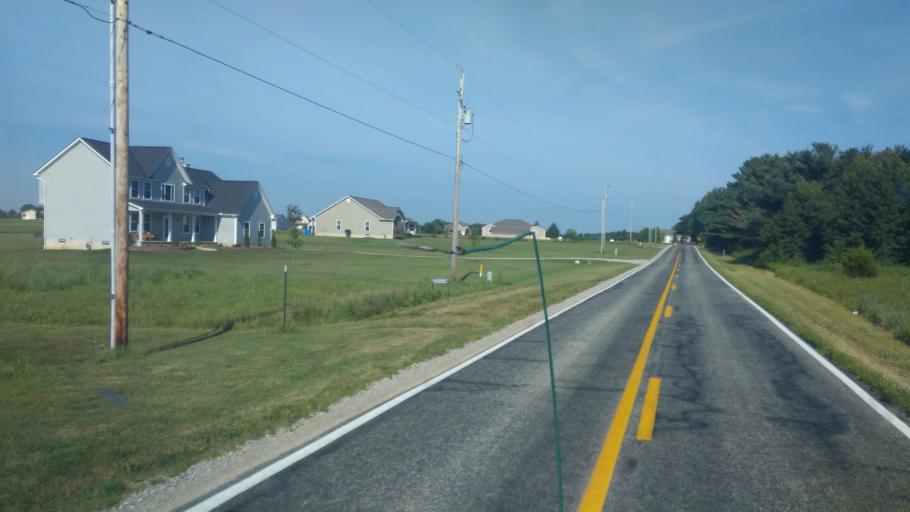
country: US
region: Ohio
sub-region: Delaware County
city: Delaware
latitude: 40.3503
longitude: -83.0501
